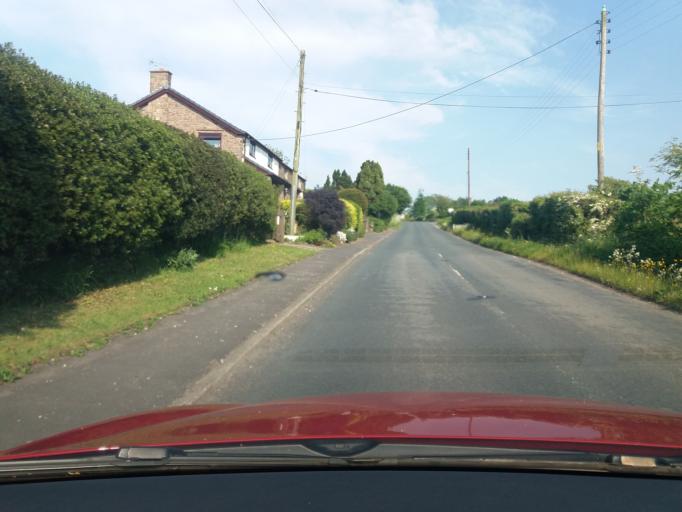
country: GB
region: England
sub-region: Lancashire
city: Chorley
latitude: 53.6853
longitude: -2.5950
